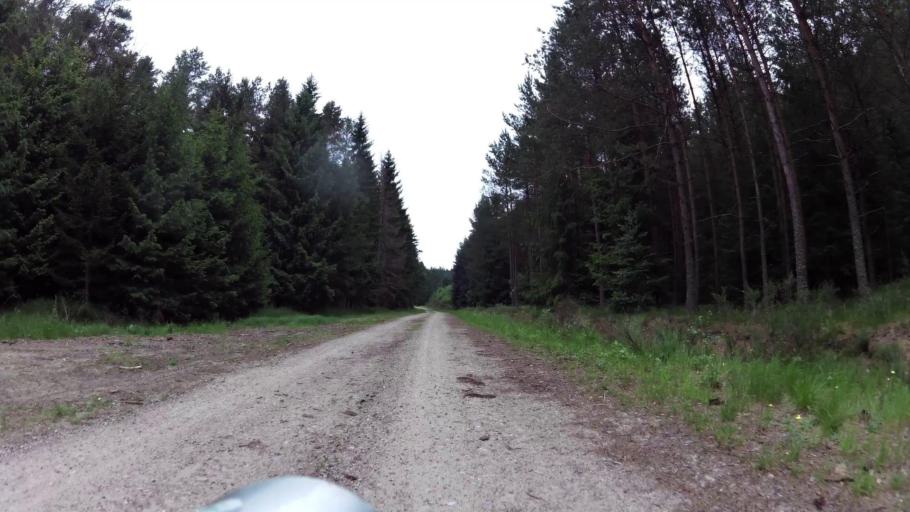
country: PL
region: West Pomeranian Voivodeship
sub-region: Powiat szczecinecki
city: Bialy Bor
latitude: 53.9471
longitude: 16.8287
